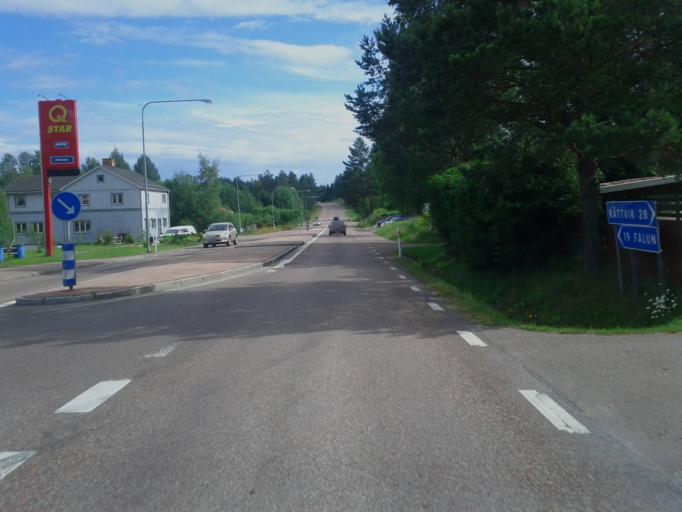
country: SE
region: Dalarna
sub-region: Faluns Kommun
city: Bjursas
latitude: 60.7339
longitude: 15.4382
